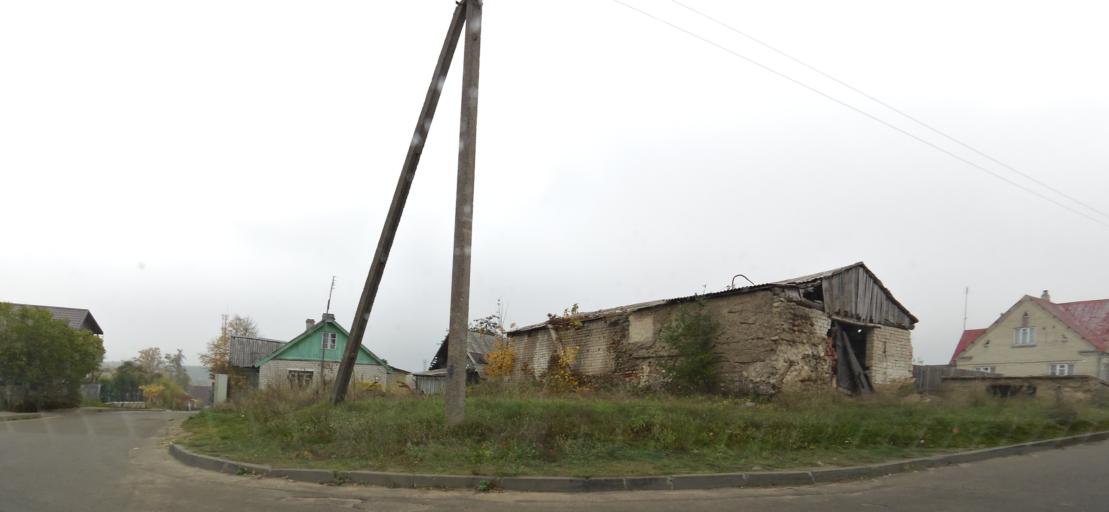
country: BY
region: Grodnenskaya
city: Astravyets
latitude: 54.6376
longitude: 25.6858
